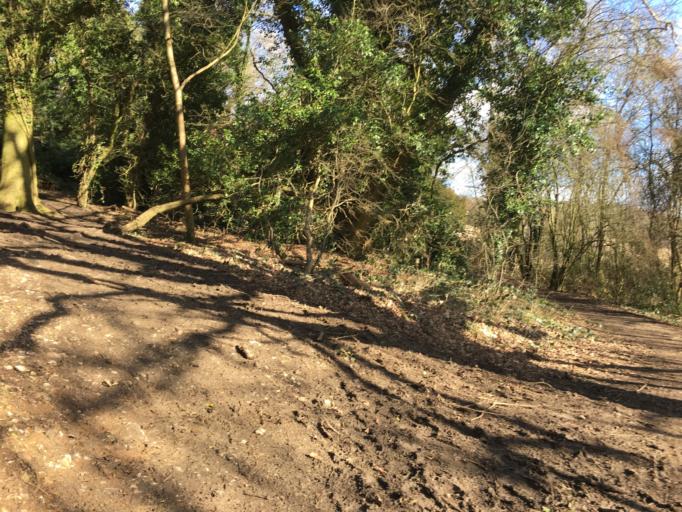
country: GB
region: England
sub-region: Surrey
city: Mickleham
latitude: 51.2475
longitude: -0.3101
